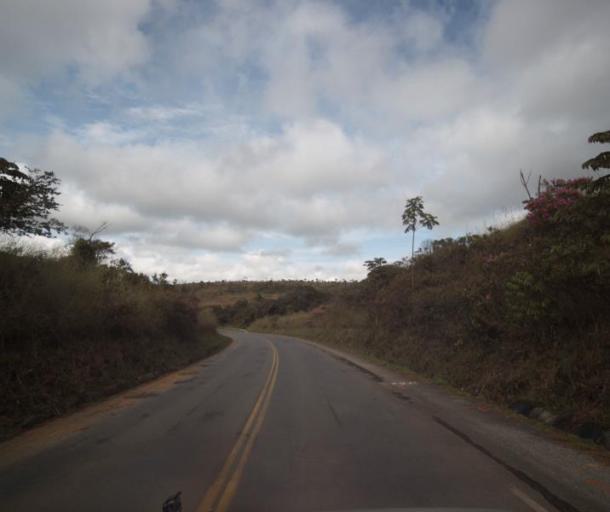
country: BR
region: Goias
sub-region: Pirenopolis
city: Pirenopolis
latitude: -15.8301
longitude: -48.7801
